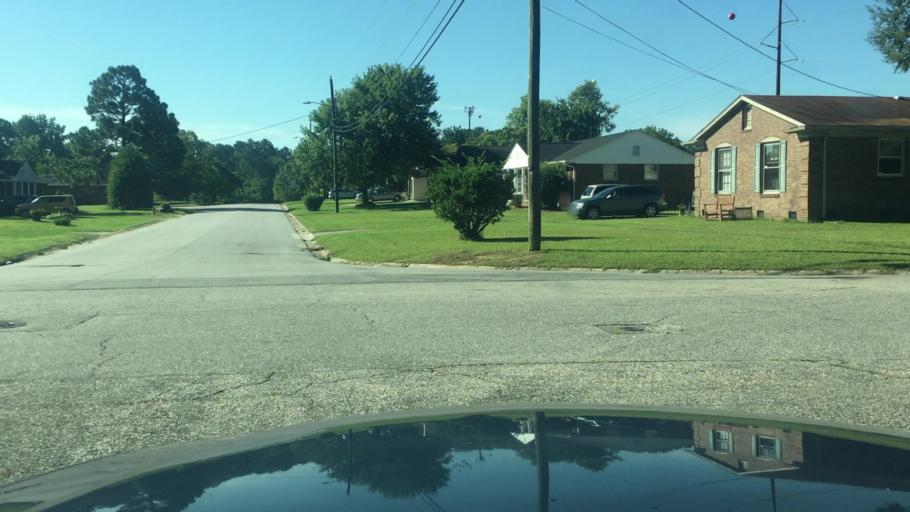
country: US
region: North Carolina
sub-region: Cumberland County
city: Spring Lake
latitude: 35.1357
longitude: -78.8947
